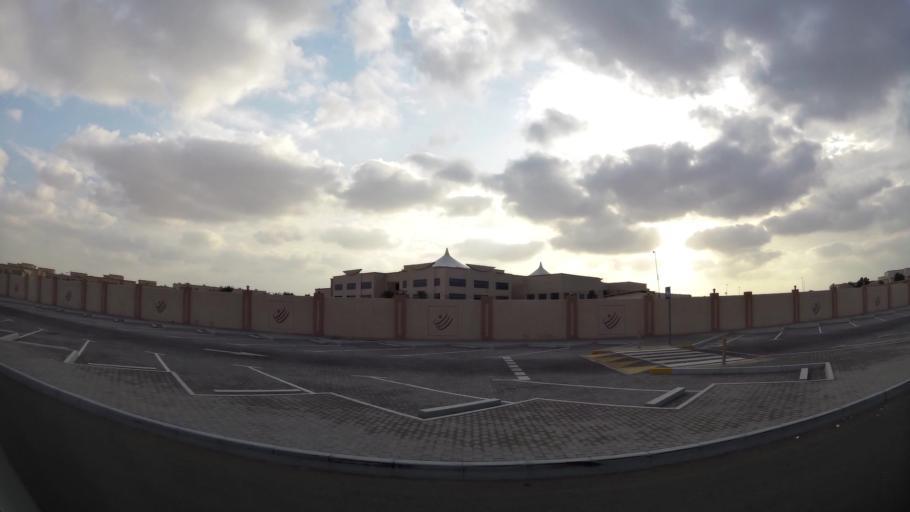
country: AE
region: Abu Dhabi
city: Abu Dhabi
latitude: 24.3627
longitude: 54.5537
